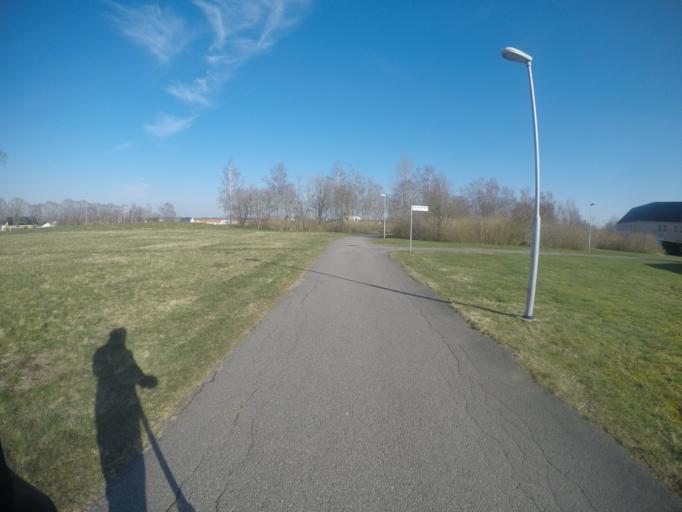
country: SE
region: Halland
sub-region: Laholms Kommun
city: Laholm
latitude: 56.5025
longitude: 13.0617
